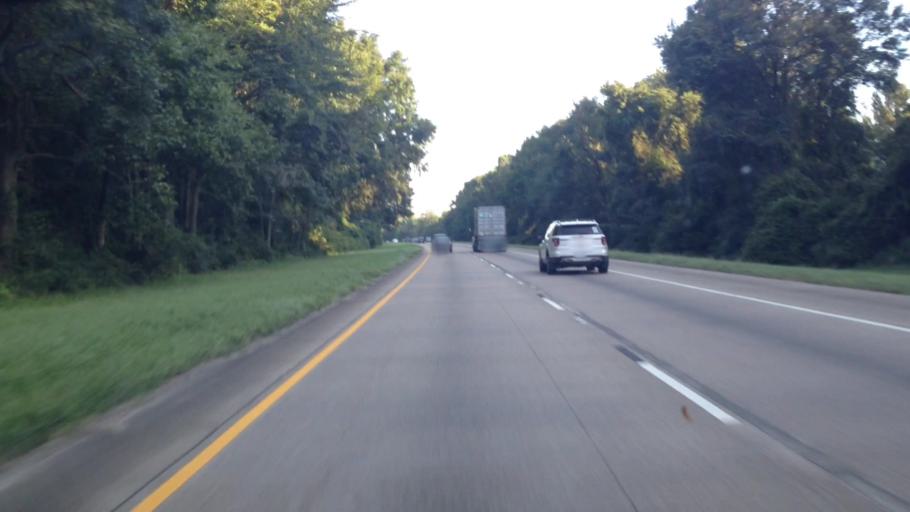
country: US
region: Louisiana
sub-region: Ascension Parish
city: Prairieville
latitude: 30.3092
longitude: -90.9949
